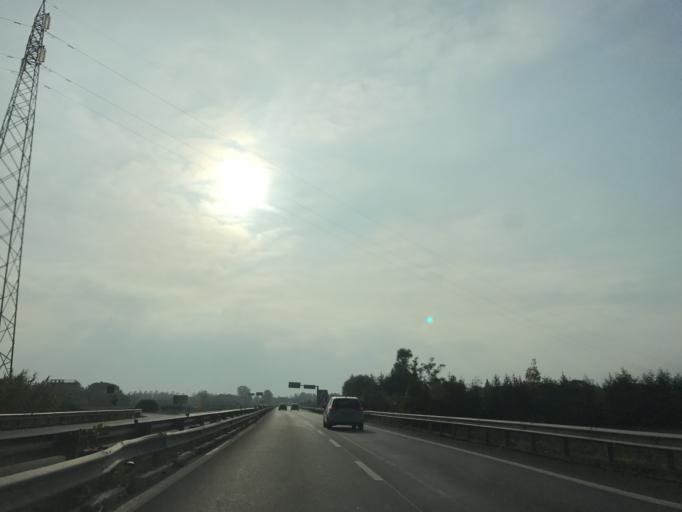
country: IT
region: Emilia-Romagna
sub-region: Provincia di Rimini
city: Bellaria-Igea Marina
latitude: 44.1148
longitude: 12.4769
